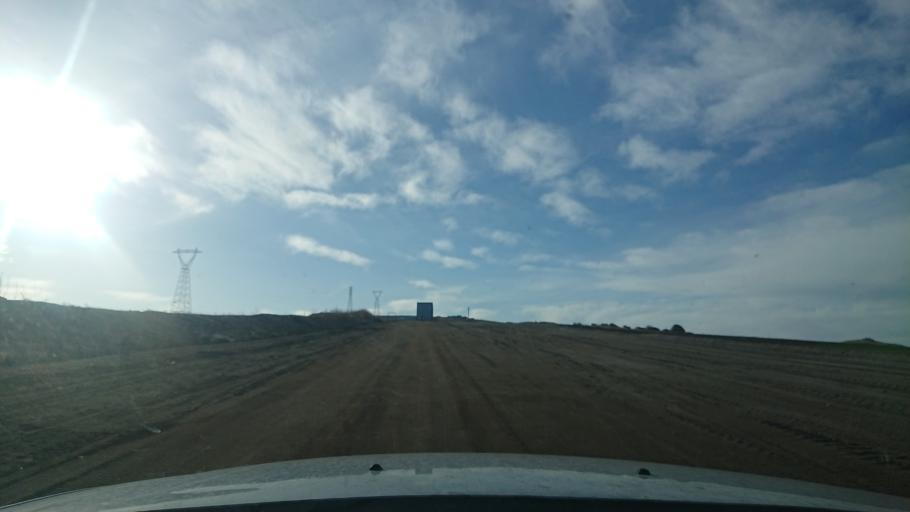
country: TR
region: Aksaray
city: Agacoren
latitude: 38.8500
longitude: 33.9430
